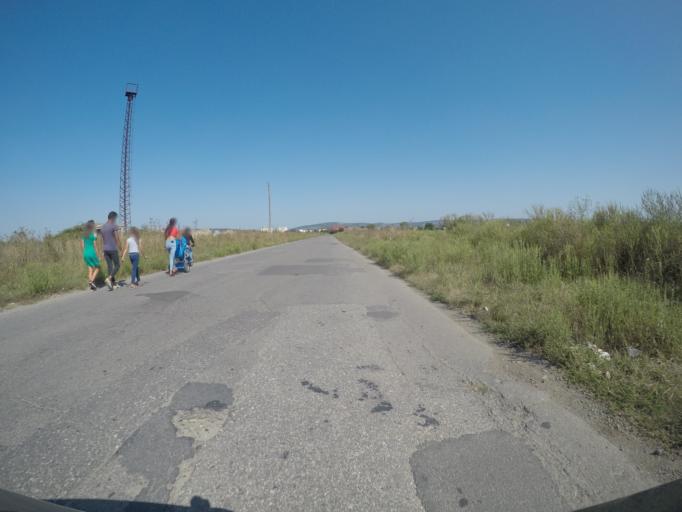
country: RO
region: Brasov
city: Fogarasch
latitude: 45.8211
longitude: 24.9801
